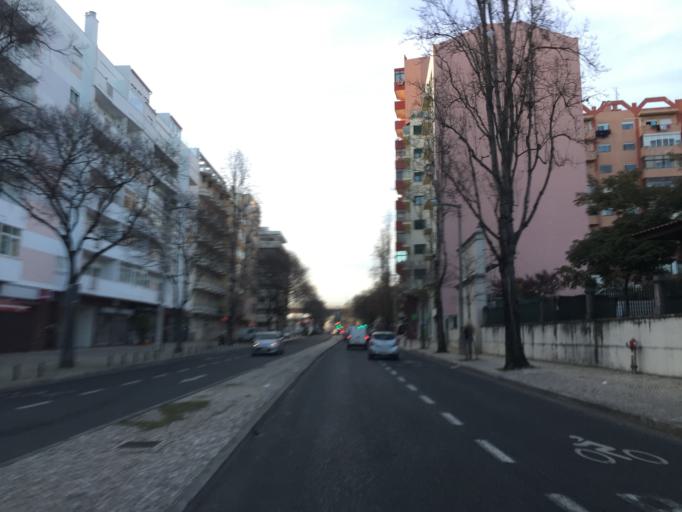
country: PT
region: Lisbon
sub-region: Odivelas
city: Olival do Basto
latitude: 38.7708
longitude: -9.1600
